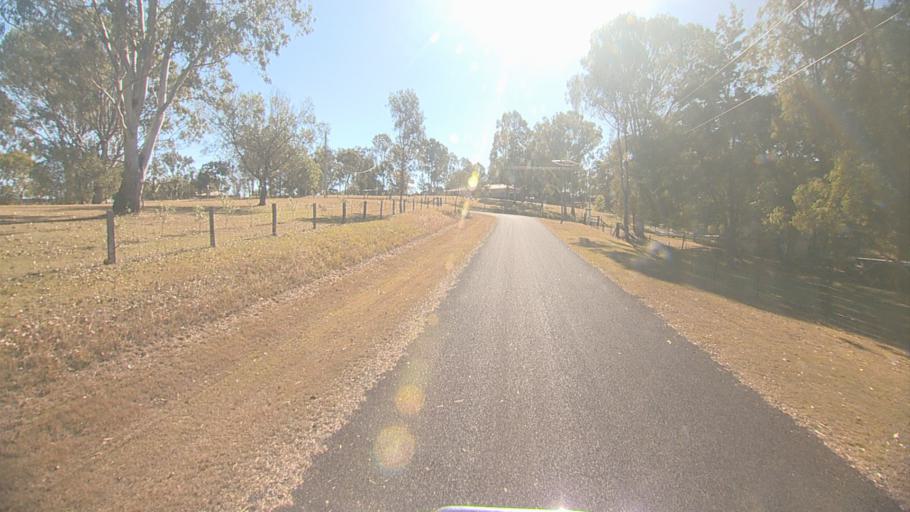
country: AU
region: Queensland
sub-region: Logan
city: Cedar Vale
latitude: -27.8935
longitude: 152.9788
